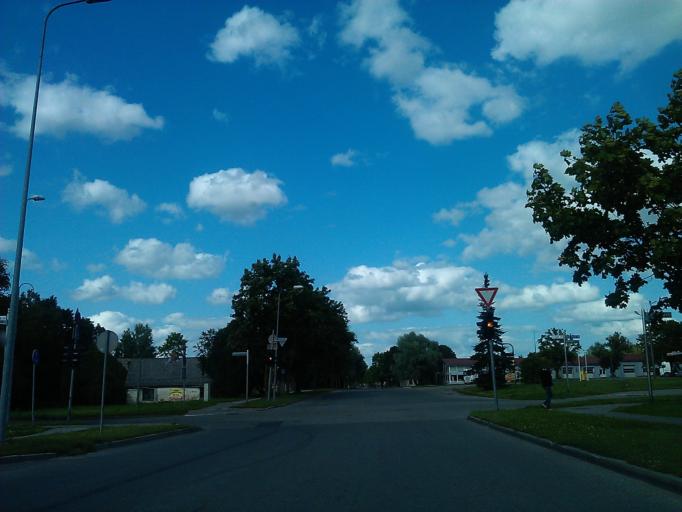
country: LV
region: Cesu Rajons
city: Cesis
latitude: 57.3072
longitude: 25.2821
